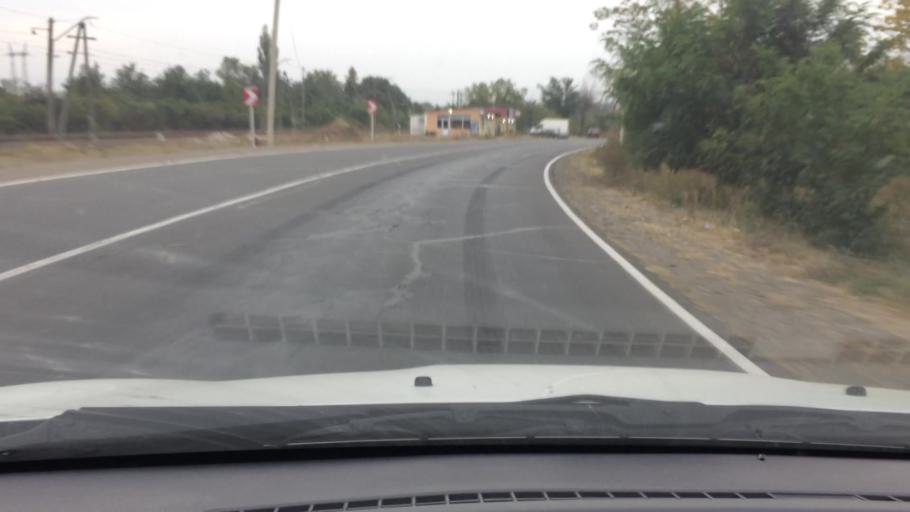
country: GE
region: Kvemo Kartli
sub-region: Marneuli
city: Marneuli
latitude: 41.4099
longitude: 44.8314
